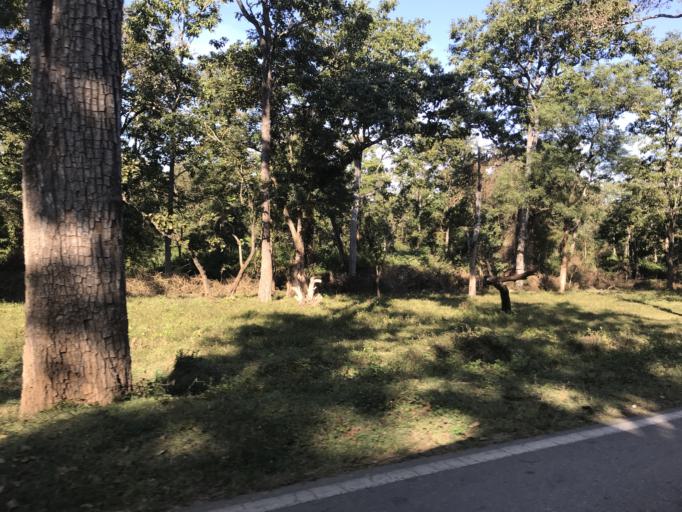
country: IN
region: Karnataka
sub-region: Mysore
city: Heggadadevankote
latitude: 11.9450
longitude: 76.2326
